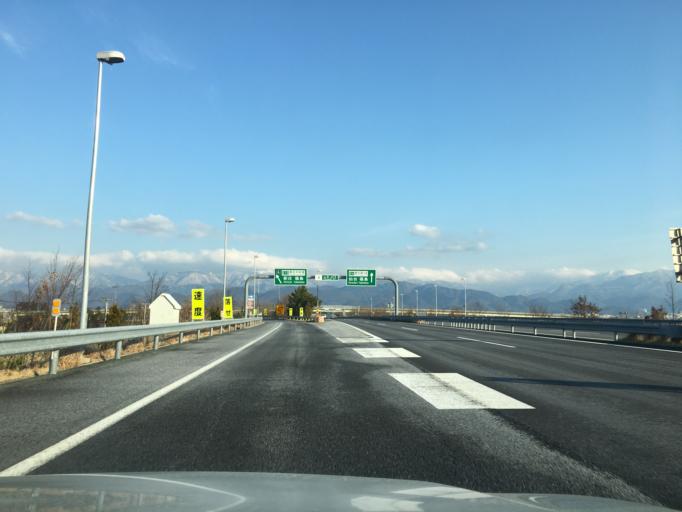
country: JP
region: Yamagata
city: Sagae
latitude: 38.3140
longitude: 140.3104
